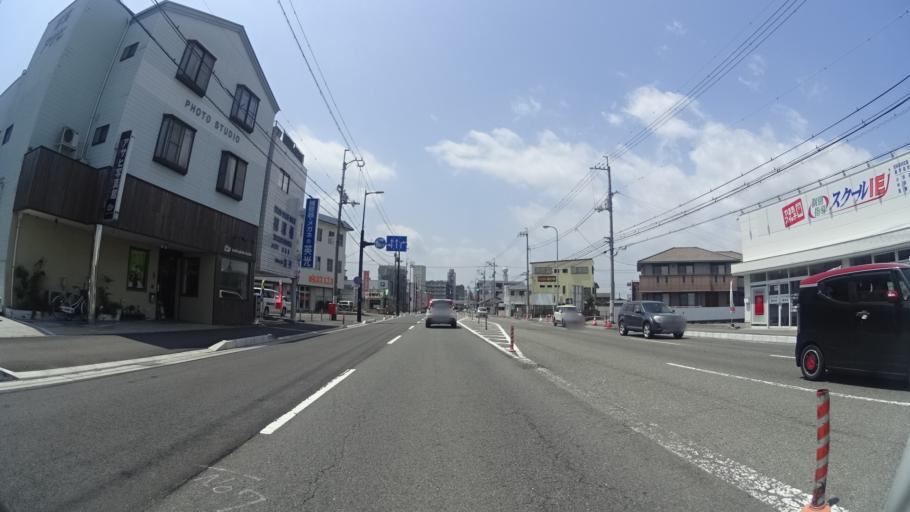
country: JP
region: Tokushima
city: Tokushima-shi
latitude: 34.0735
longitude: 134.5095
